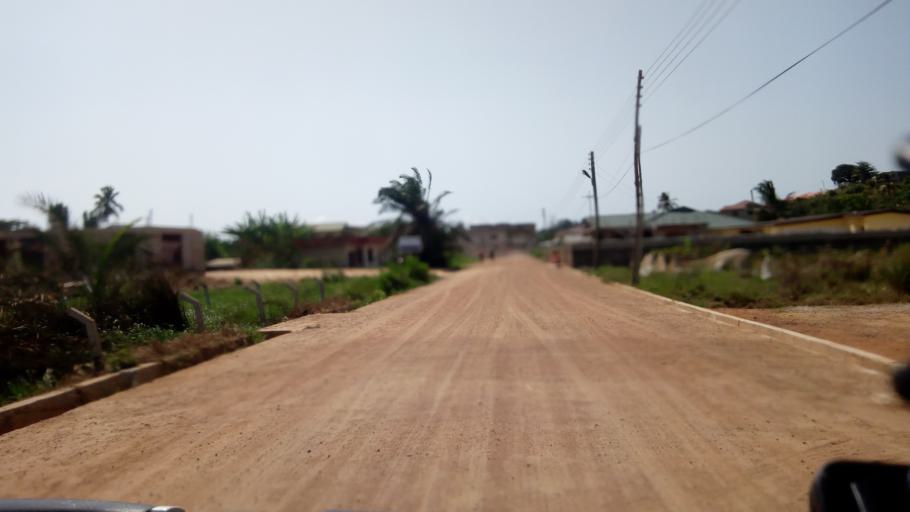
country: GH
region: Central
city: Cape Coast
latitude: 5.1140
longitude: -1.2690
